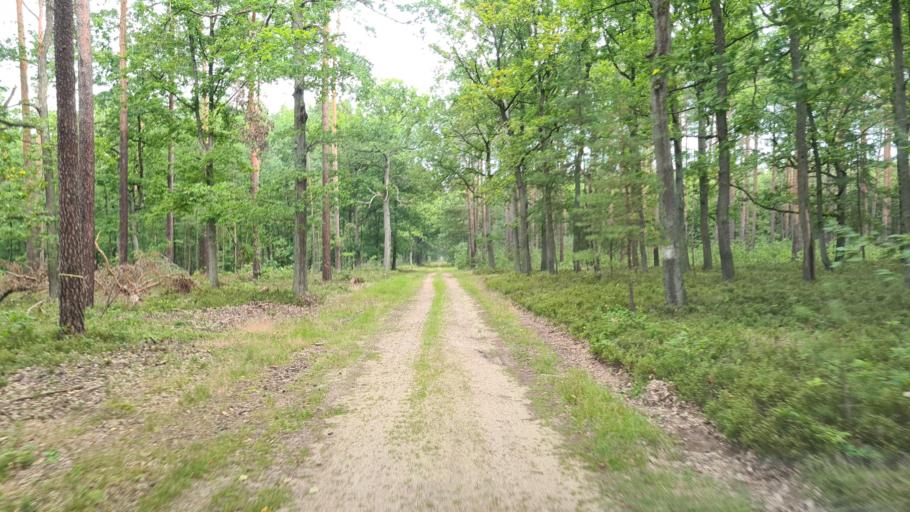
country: DE
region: Brandenburg
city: Hohenbucko
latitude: 51.7811
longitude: 13.5459
